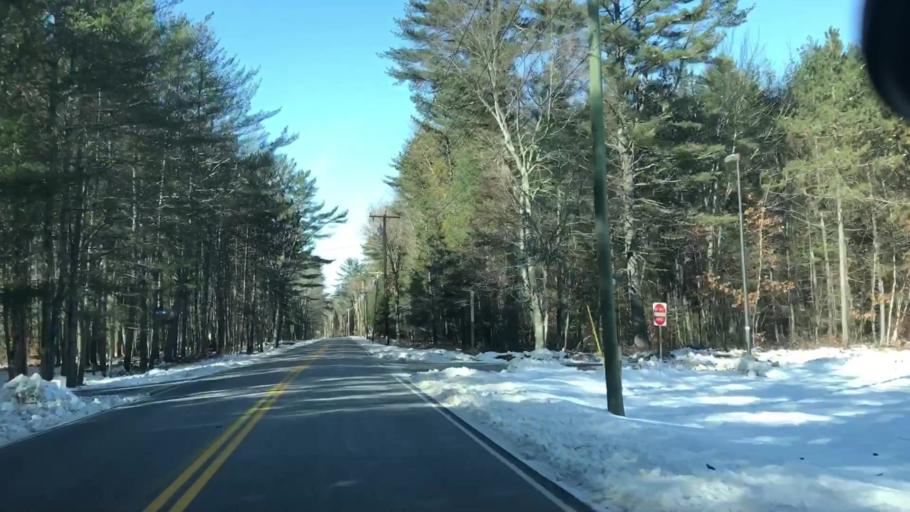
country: US
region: Maine
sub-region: Oxford County
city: Brownfield
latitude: 43.9631
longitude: -70.8617
